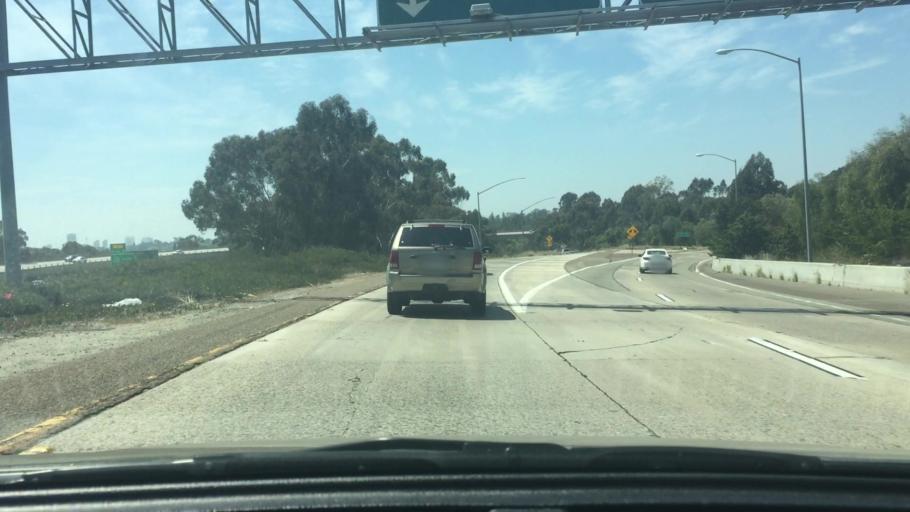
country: US
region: California
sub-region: San Diego County
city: National City
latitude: 32.7195
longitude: -117.0994
